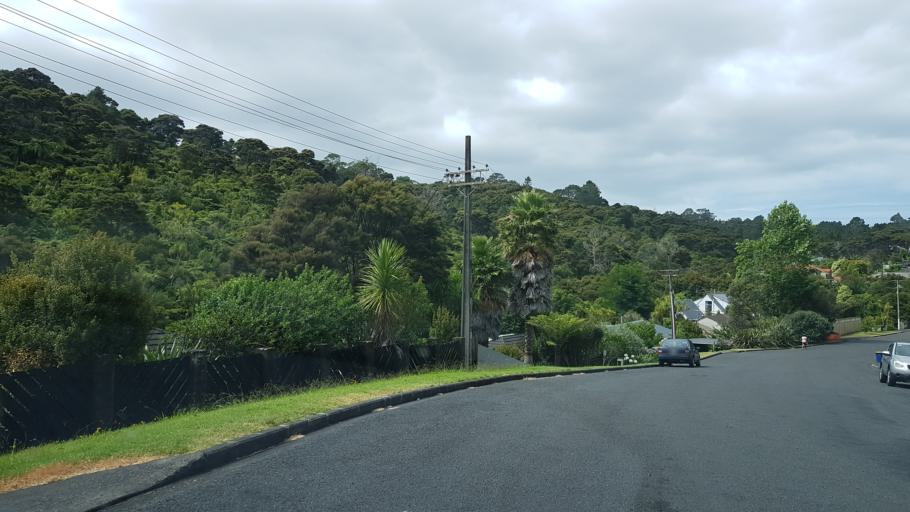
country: NZ
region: Auckland
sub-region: Auckland
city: North Shore
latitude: -36.7708
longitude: 174.7049
